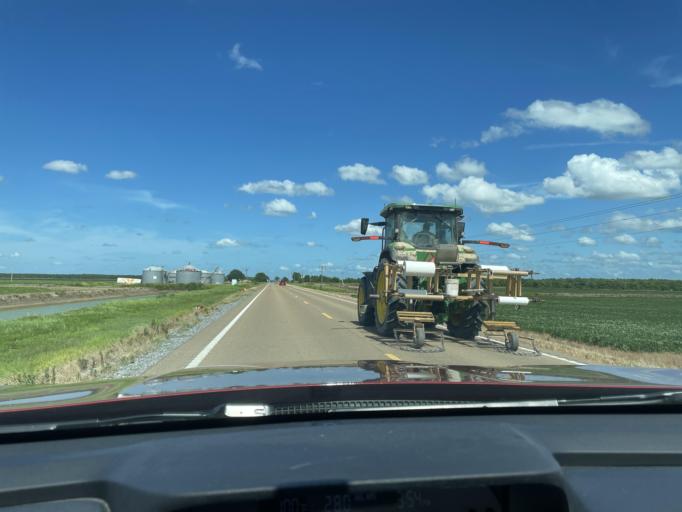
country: US
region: Mississippi
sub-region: Humphreys County
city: Belzoni
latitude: 33.1830
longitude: -90.6526
